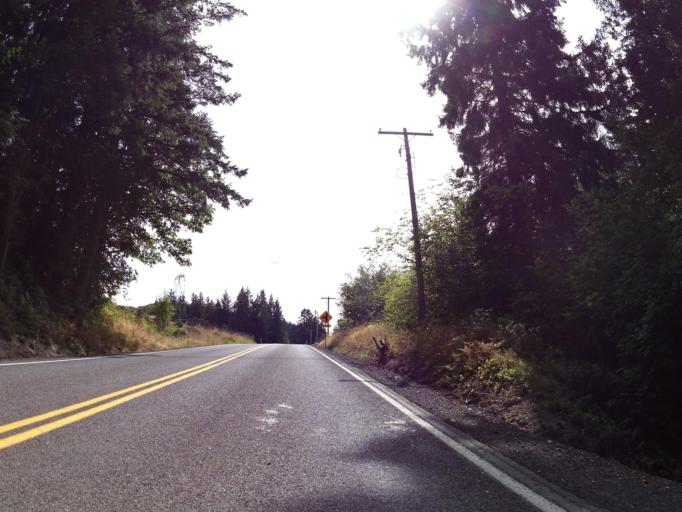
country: US
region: Washington
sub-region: Lewis County
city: Napavine
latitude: 46.5743
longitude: -122.9711
